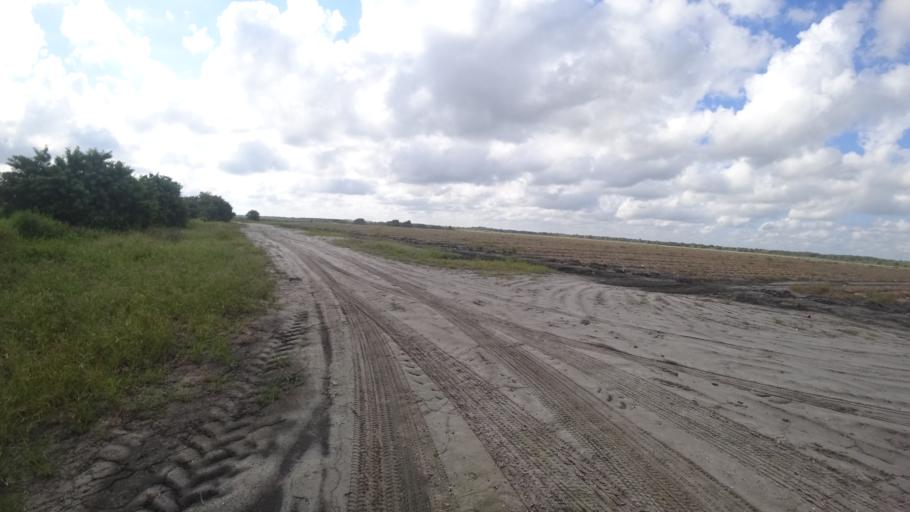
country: US
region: Florida
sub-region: Sarasota County
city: Lake Sarasota
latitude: 27.4406
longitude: -82.1832
